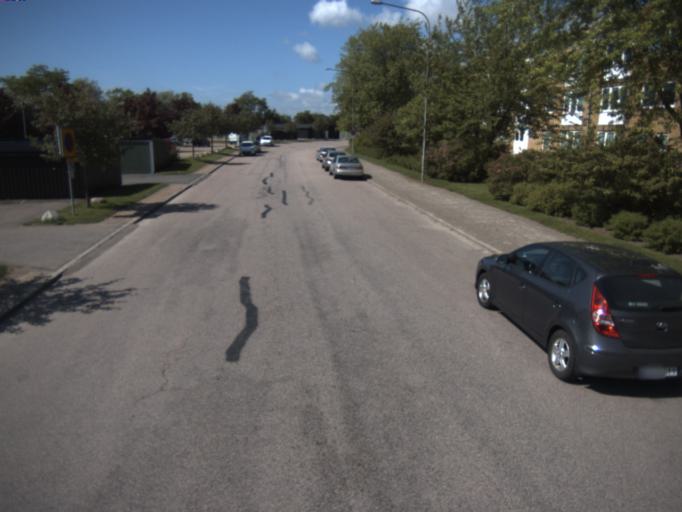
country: SE
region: Skane
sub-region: Helsingborg
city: Helsingborg
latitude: 56.0701
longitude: 12.7036
